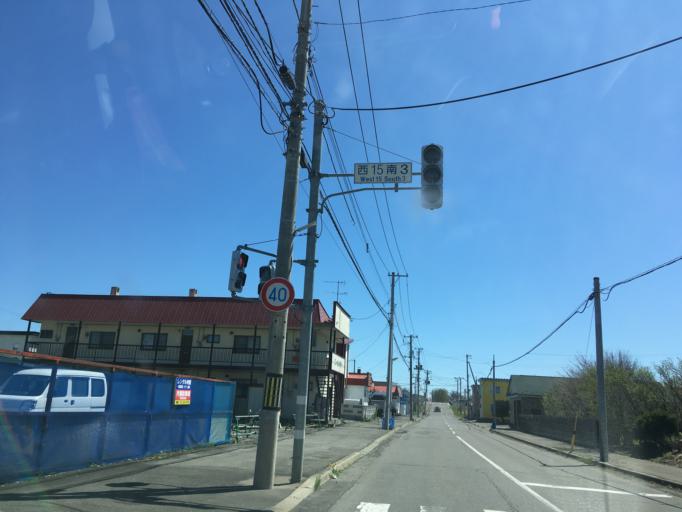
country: JP
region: Hokkaido
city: Obihiro
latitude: 42.9276
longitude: 143.1773
